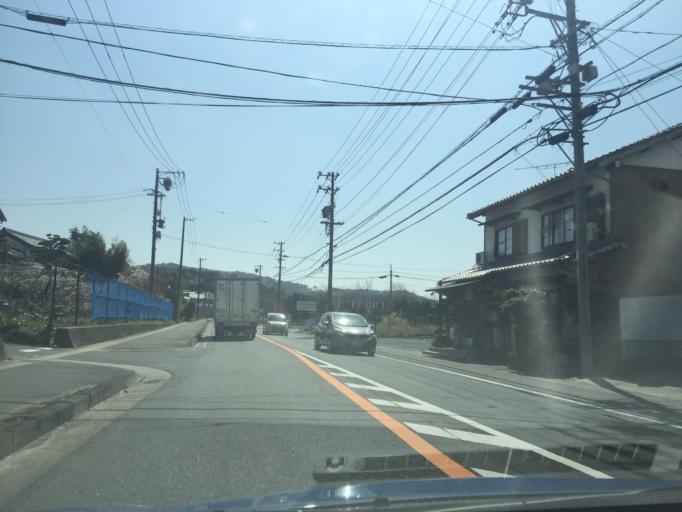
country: JP
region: Shizuoka
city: Hamamatsu
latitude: 34.7928
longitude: 137.6480
